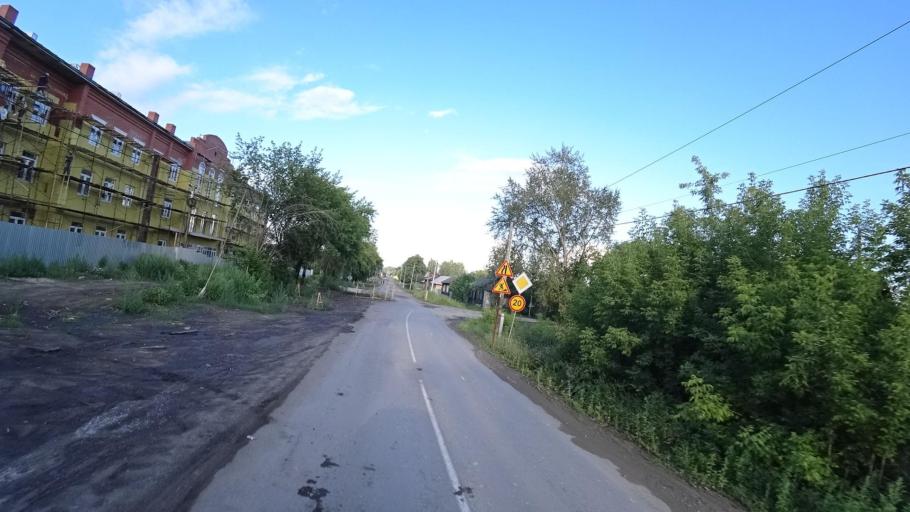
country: RU
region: Sverdlovsk
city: Kamyshlov
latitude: 56.8486
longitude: 62.7061
